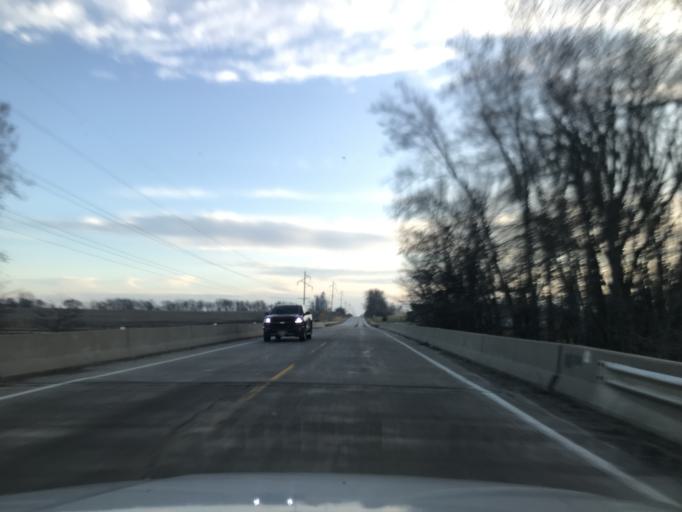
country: US
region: Illinois
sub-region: Mercer County
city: Aledo
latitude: 41.0436
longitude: -90.7459
